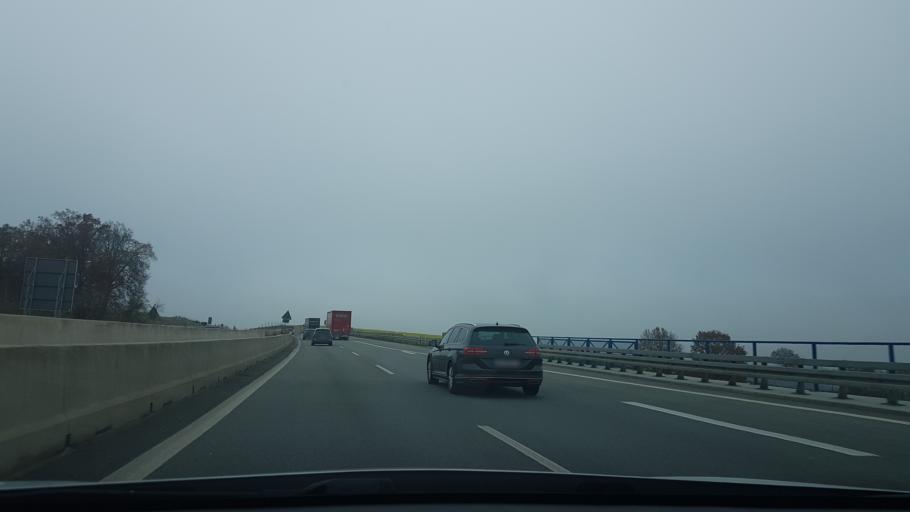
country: DE
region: Bavaria
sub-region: Lower Bavaria
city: Ergoldsbach
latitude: 48.6727
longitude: 12.1914
